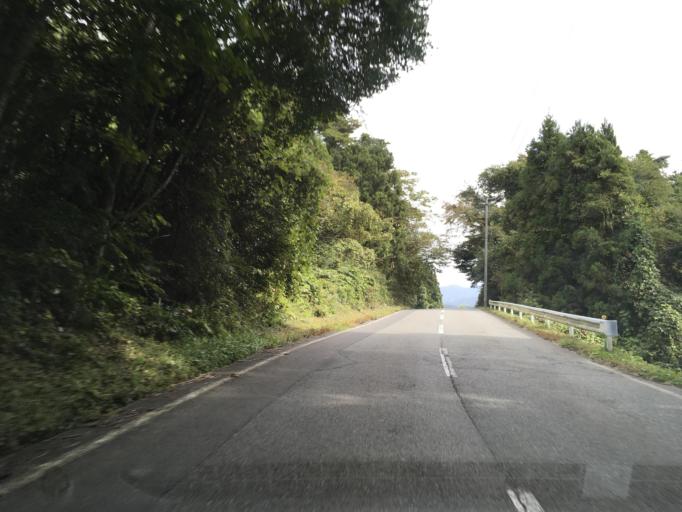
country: JP
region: Iwate
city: Mizusawa
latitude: 39.0408
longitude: 141.3139
